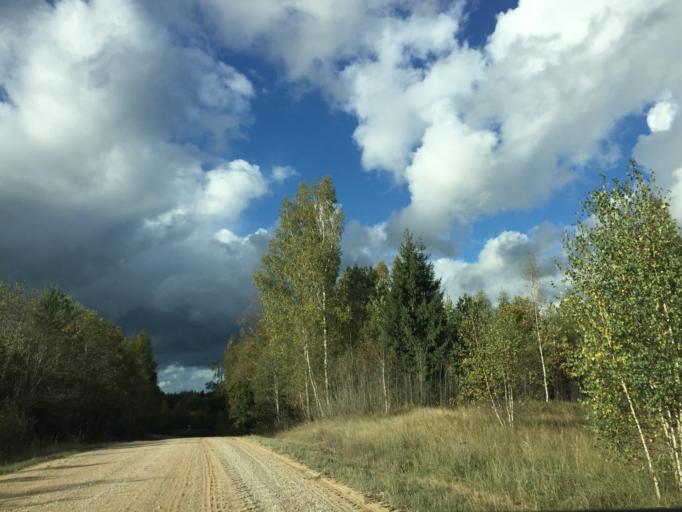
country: LV
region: Malpils
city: Malpils
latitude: 57.0305
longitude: 25.0517
